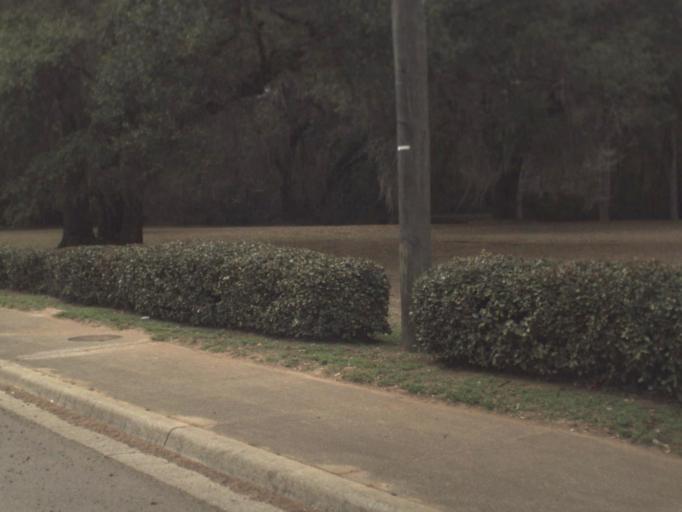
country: US
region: Florida
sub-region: Leon County
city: Tallahassee
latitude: 30.5330
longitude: -84.2331
